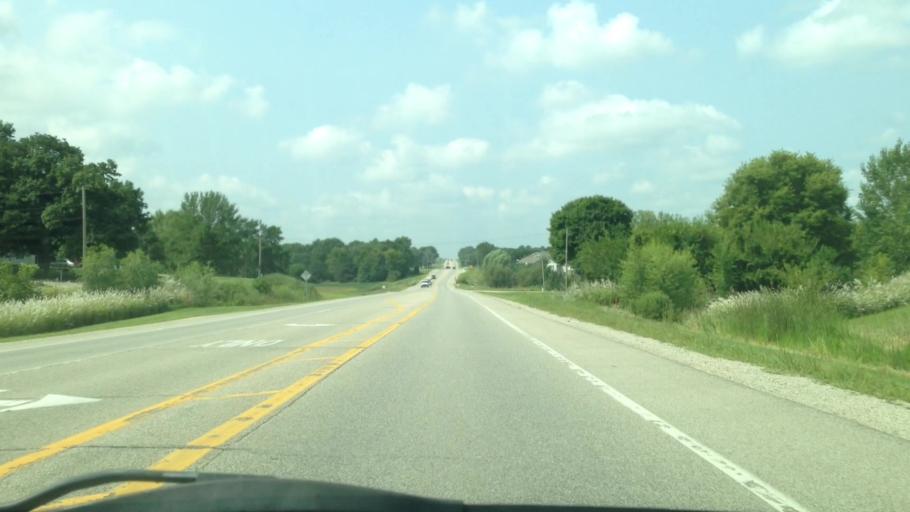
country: US
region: Iowa
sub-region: Linn County
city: Fairfax
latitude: 41.9421
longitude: -91.7484
